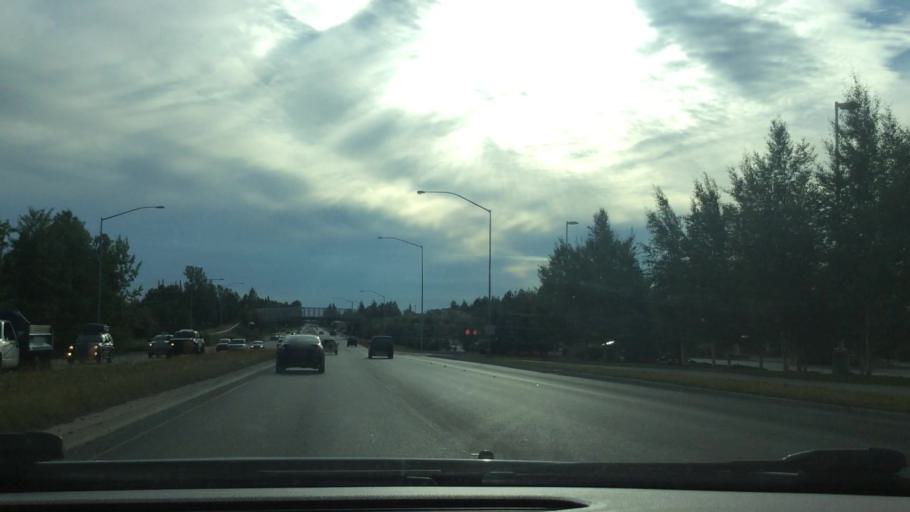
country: US
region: Alaska
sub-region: Anchorage Municipality
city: Anchorage
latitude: 61.1807
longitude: -149.8018
